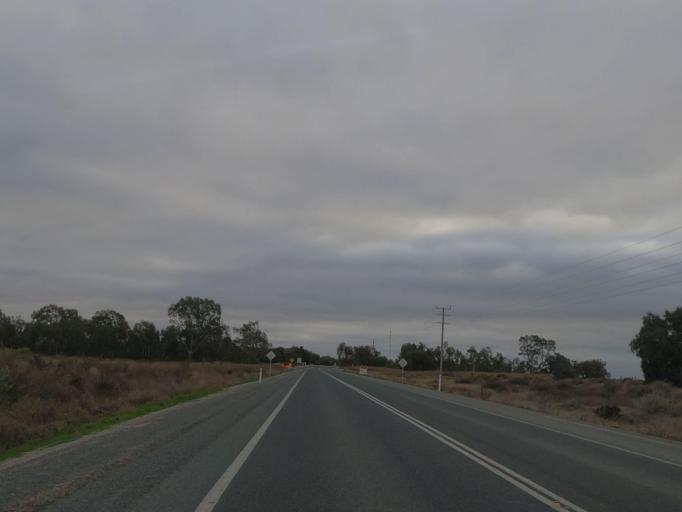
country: AU
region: Victoria
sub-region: Swan Hill
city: Swan Hill
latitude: -35.5375
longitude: 143.7478
